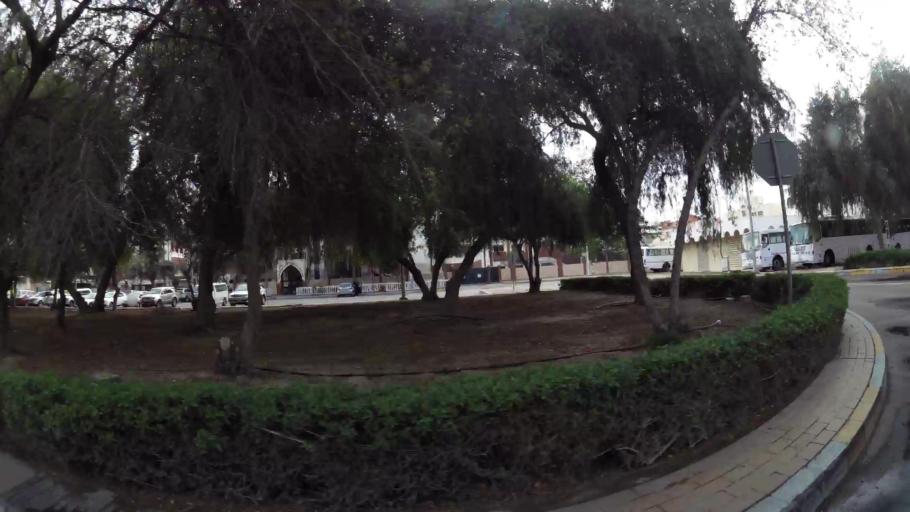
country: AE
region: Abu Dhabi
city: Abu Dhabi
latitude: 24.4452
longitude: 54.4091
